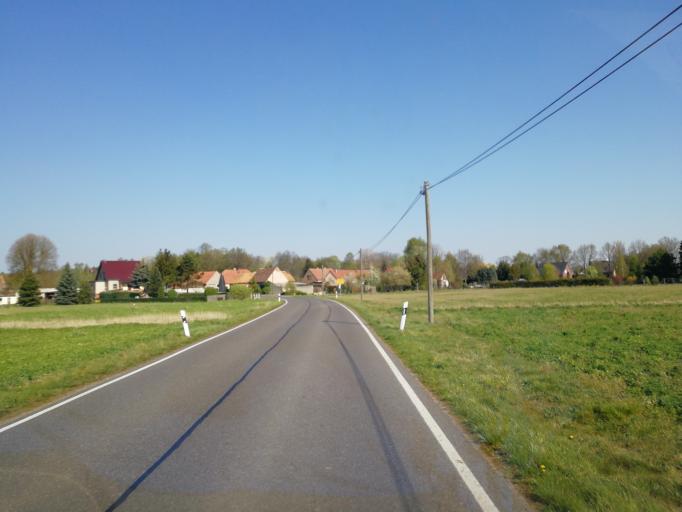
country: DE
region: Brandenburg
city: Crinitz
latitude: 51.7359
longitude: 13.8513
